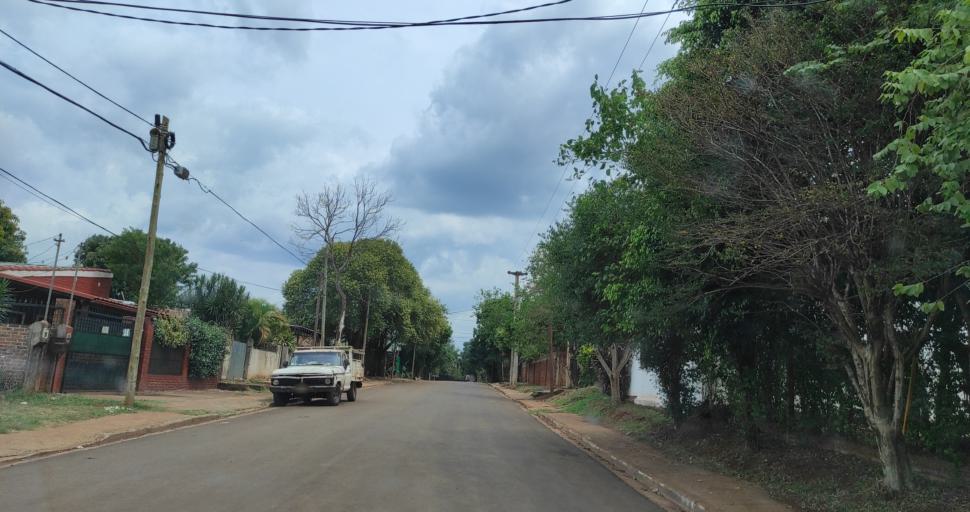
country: AR
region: Misiones
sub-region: Departamento de Capital
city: Posadas
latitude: -27.4081
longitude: -55.9189
